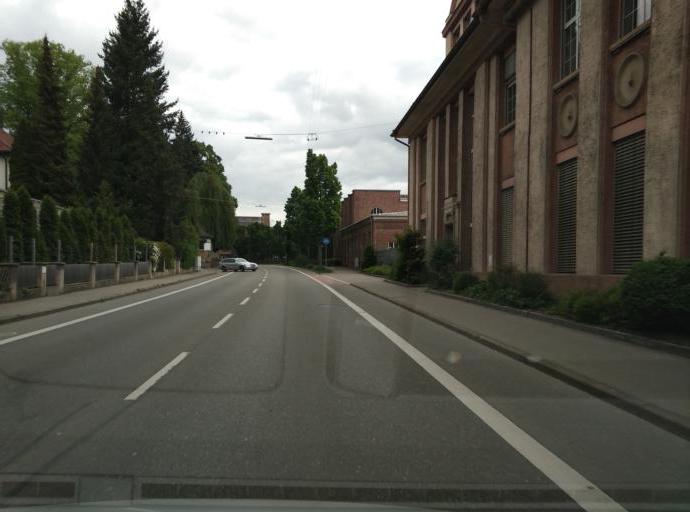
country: DE
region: Baden-Wuerttemberg
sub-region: Regierungsbezirk Stuttgart
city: Nurtingen
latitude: 48.6213
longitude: 9.3430
